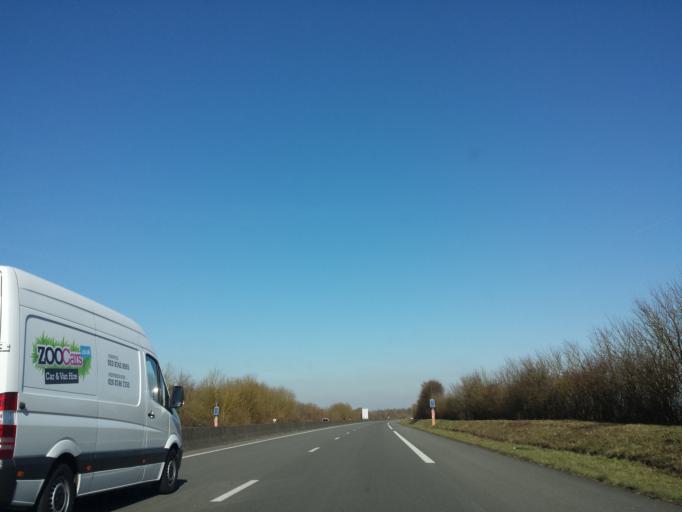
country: FR
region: Picardie
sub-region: Departement de l'Oise
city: Breteuil
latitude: 49.6219
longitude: 2.2090
